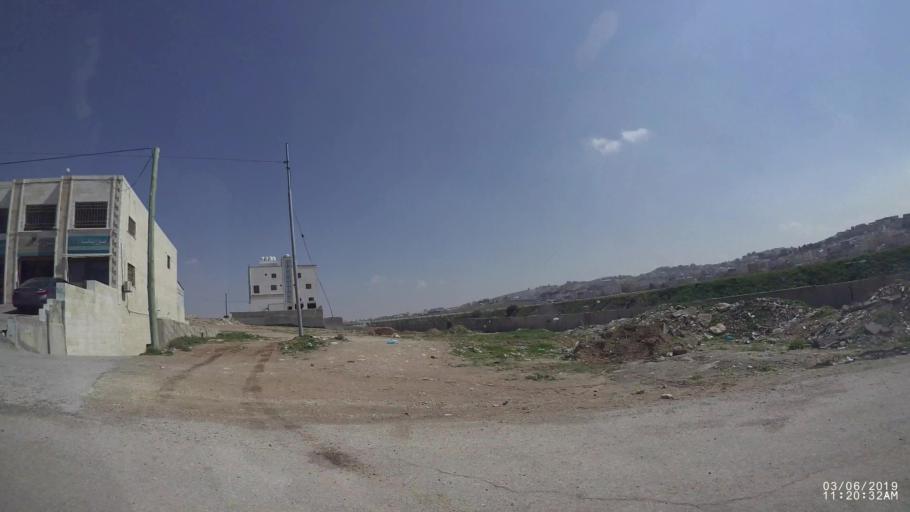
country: JO
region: Amman
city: Amman
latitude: 31.9782
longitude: 35.9992
